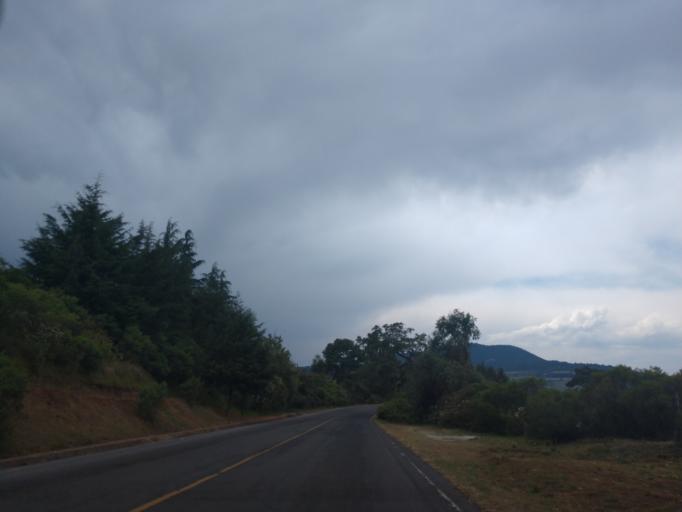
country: MX
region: Jalisco
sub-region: Mazamitla
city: Mazamitla
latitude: 19.9218
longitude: -103.0376
